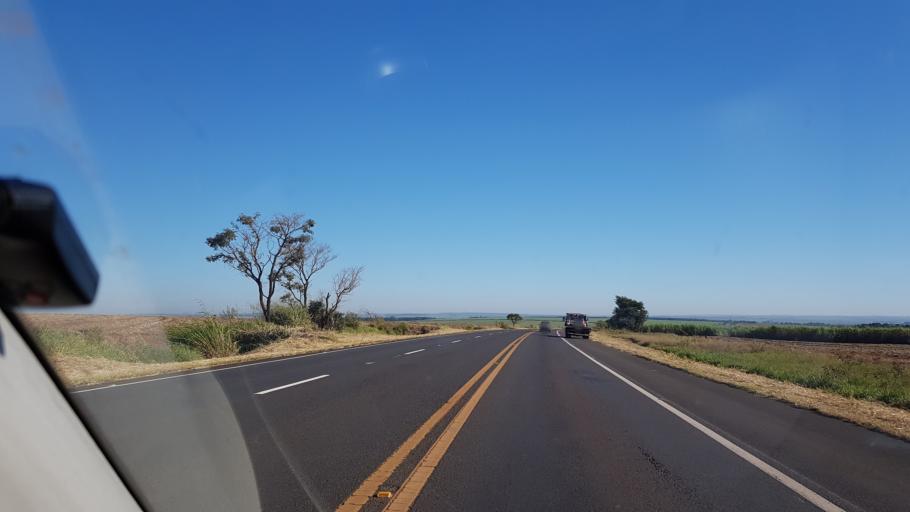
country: BR
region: Sao Paulo
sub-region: Assis
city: Assis
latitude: -22.5717
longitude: -50.5180
